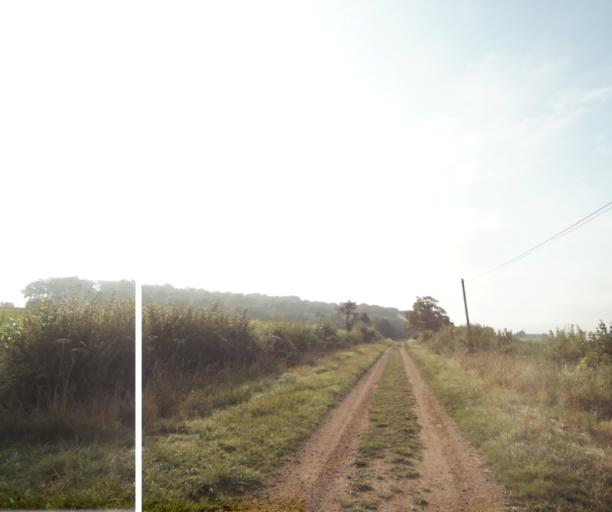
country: FR
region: Bourgogne
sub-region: Departement de Saone-et-Loire
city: Charolles
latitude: 46.4779
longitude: 4.2751
